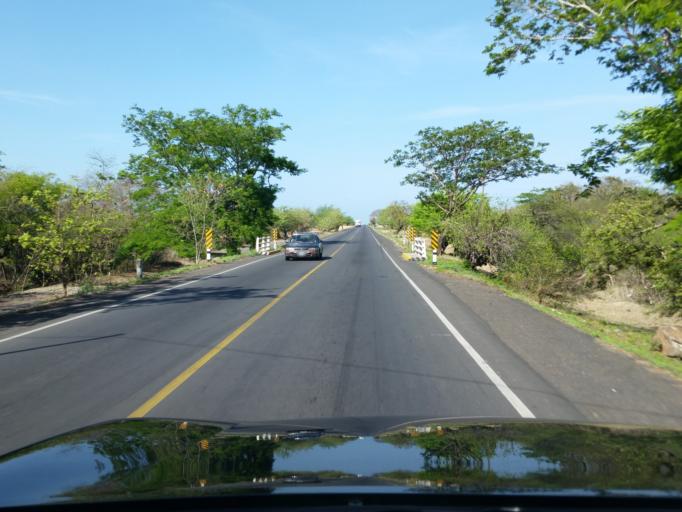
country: NI
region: Leon
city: La Paz Centro
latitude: 12.2818
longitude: -86.7242
